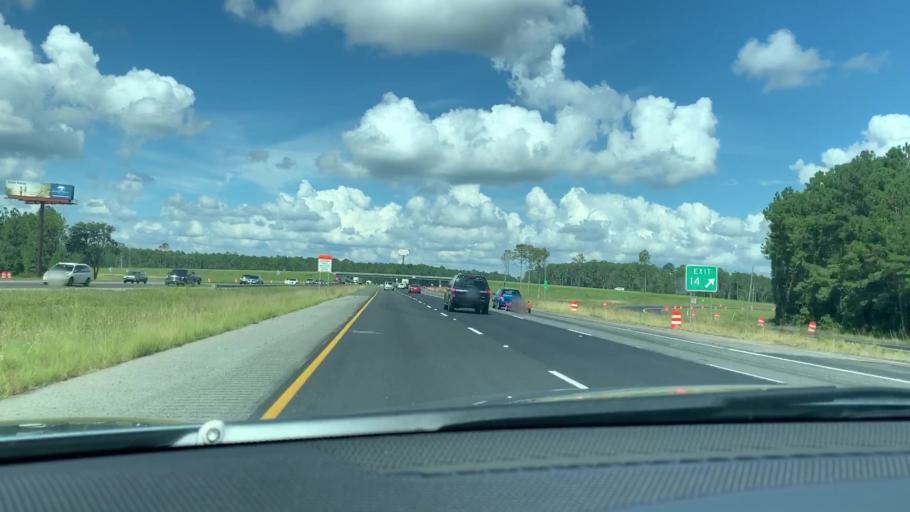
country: US
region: Georgia
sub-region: Camden County
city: Woodbine
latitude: 30.9415
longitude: -81.6863
